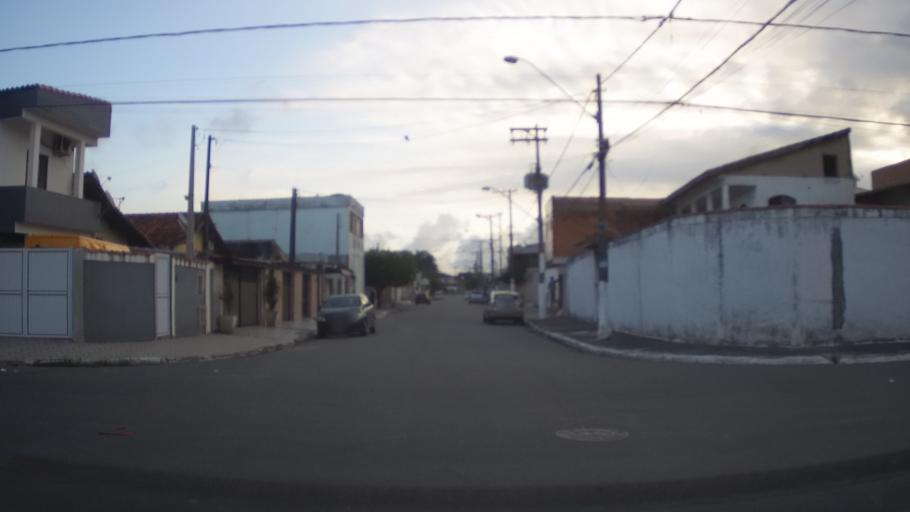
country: BR
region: Sao Paulo
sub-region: Praia Grande
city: Praia Grande
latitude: -24.0010
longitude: -46.4306
